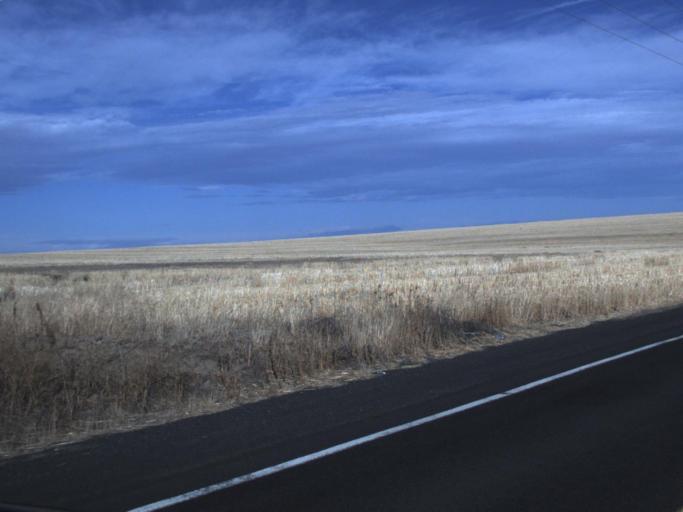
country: US
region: Washington
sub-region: Adams County
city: Ritzville
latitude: 47.1039
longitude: -118.6654
